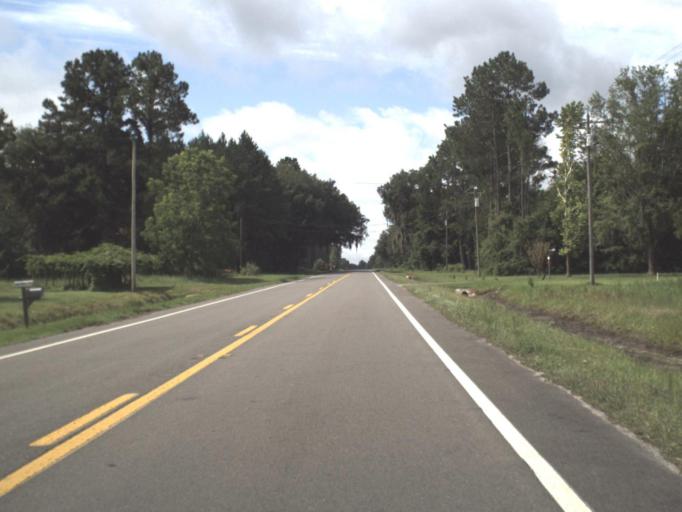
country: US
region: Florida
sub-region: Columbia County
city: Five Points
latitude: 30.2928
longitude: -82.6307
